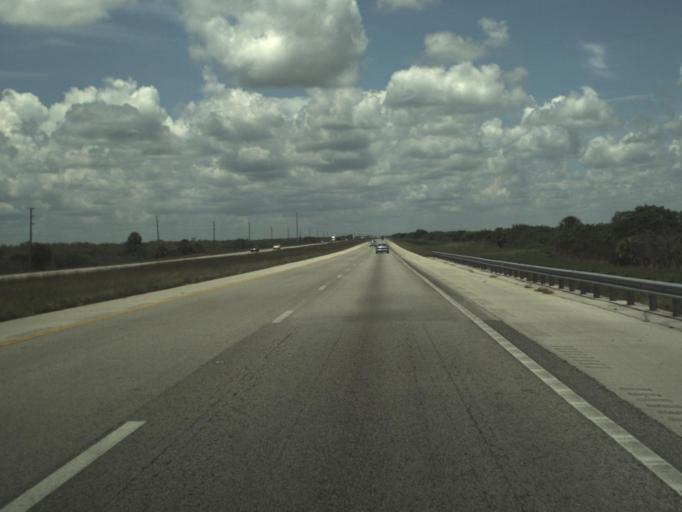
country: US
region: Florida
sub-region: Broward County
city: Weston
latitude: 26.1567
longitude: -80.7645
